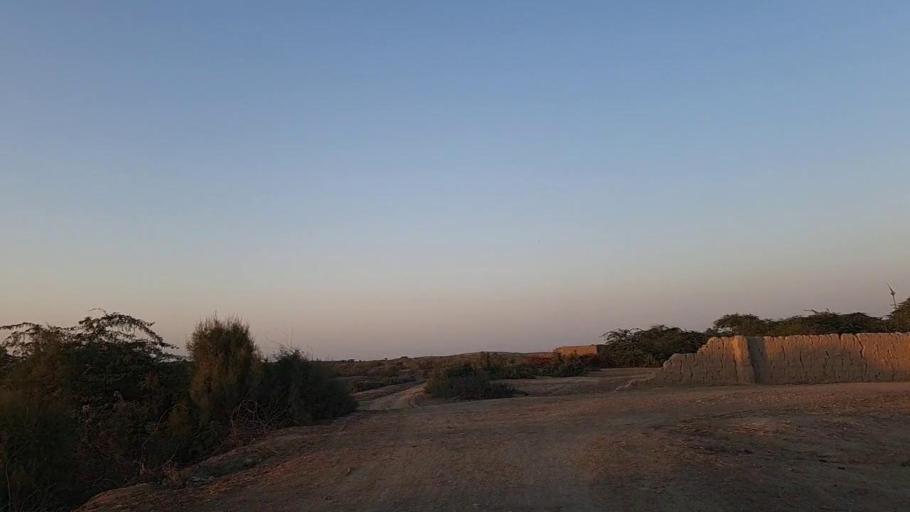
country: PK
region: Sindh
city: Jam Sahib
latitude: 26.3150
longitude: 68.6535
